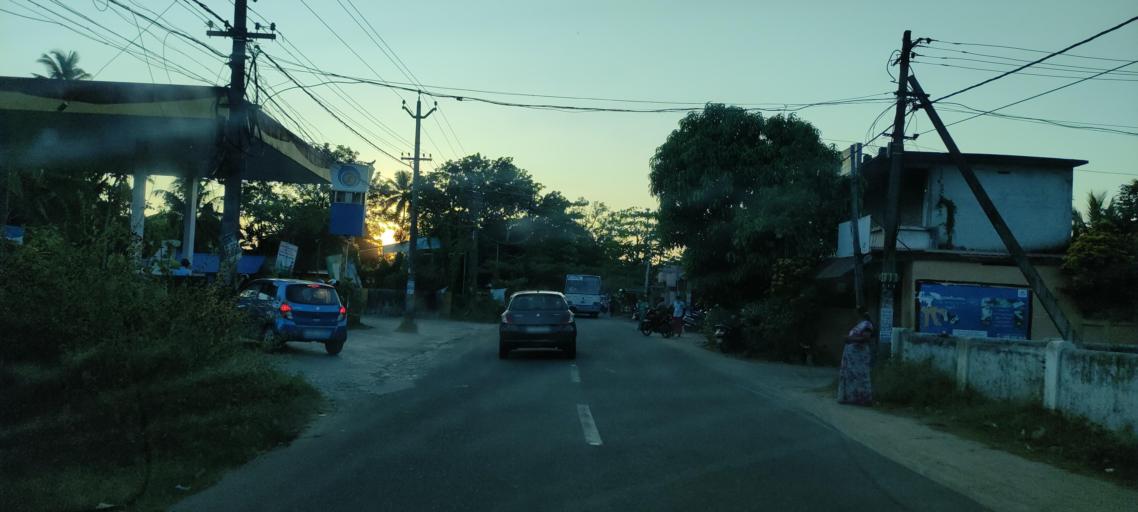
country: IN
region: Kerala
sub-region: Alappuzha
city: Kayankulam
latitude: 9.2582
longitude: 76.4274
